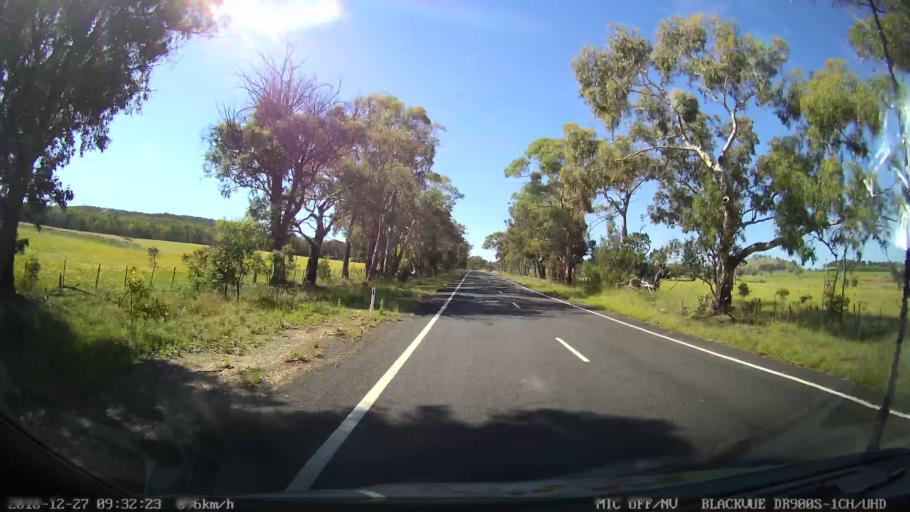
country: AU
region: New South Wales
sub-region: Lithgow
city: Portland
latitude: -33.2065
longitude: 150.0156
